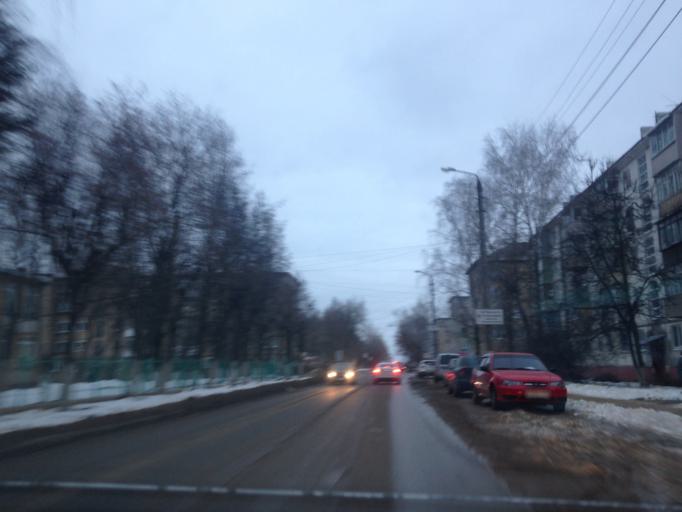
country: RU
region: Tula
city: Shchekino
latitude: 54.0124
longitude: 37.5164
